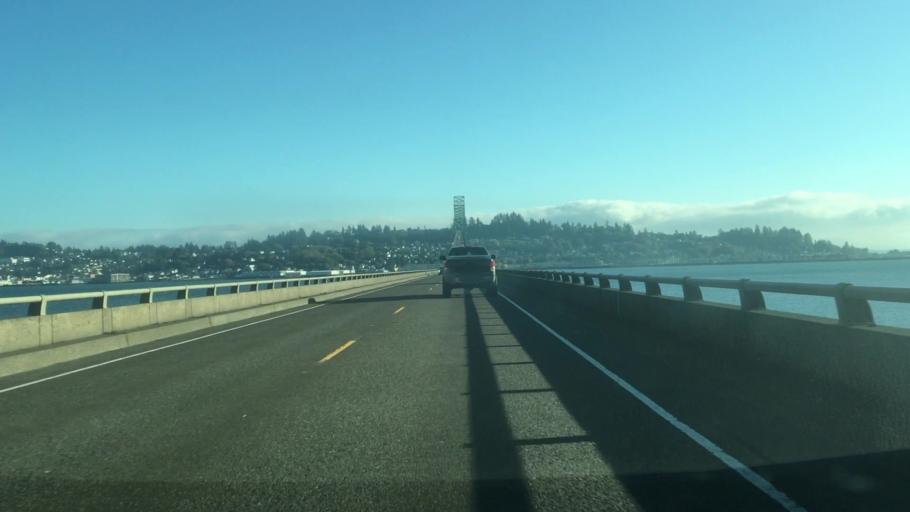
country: US
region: Oregon
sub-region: Clatsop County
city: Astoria
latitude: 46.2058
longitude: -123.8572
